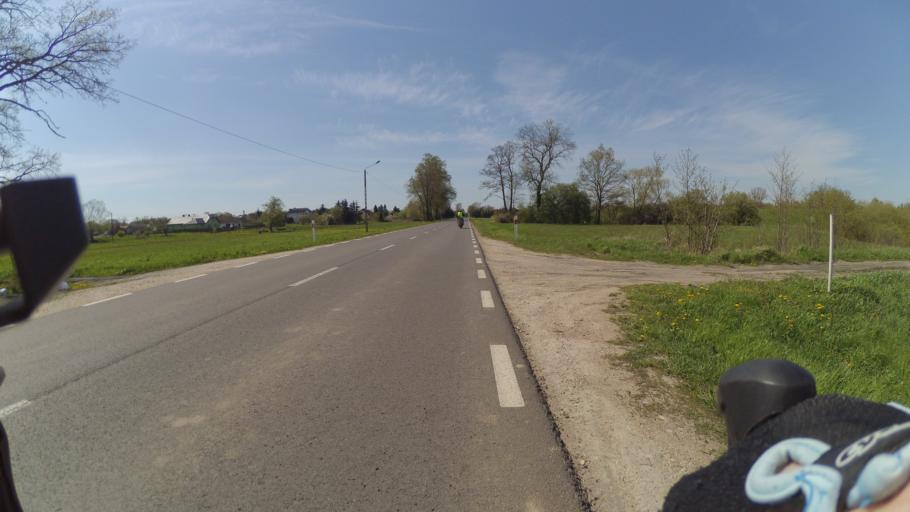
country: PL
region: Masovian Voivodeship
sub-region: Powiat plonski
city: Czerwinsk Nad Wisla
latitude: 52.3776
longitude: 20.3443
